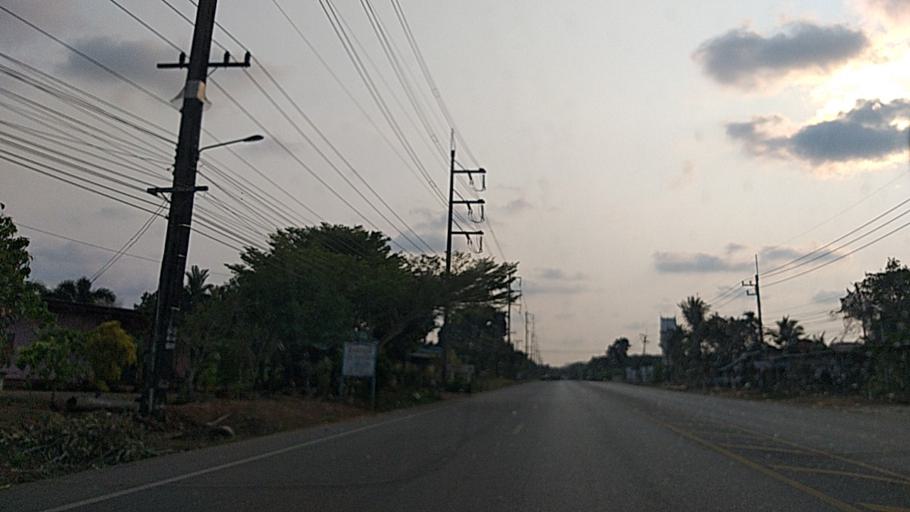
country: TH
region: Trat
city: Khao Saming
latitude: 12.3012
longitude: 102.3435
